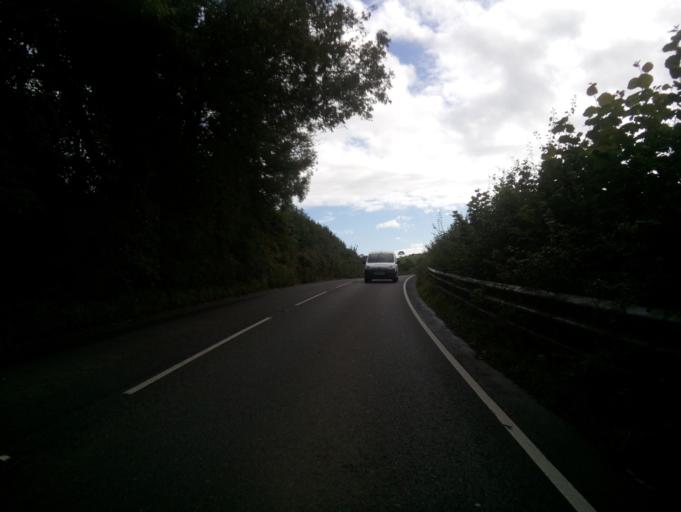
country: GB
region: England
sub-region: Devon
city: Modbury
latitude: 50.3259
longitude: -3.8426
